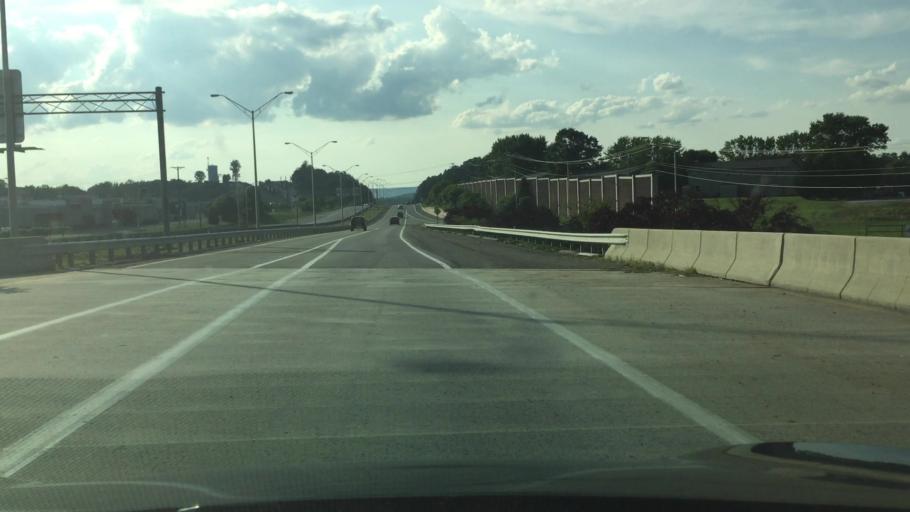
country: US
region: Virginia
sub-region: Montgomery County
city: Christiansburg
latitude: 37.1340
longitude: -80.3744
